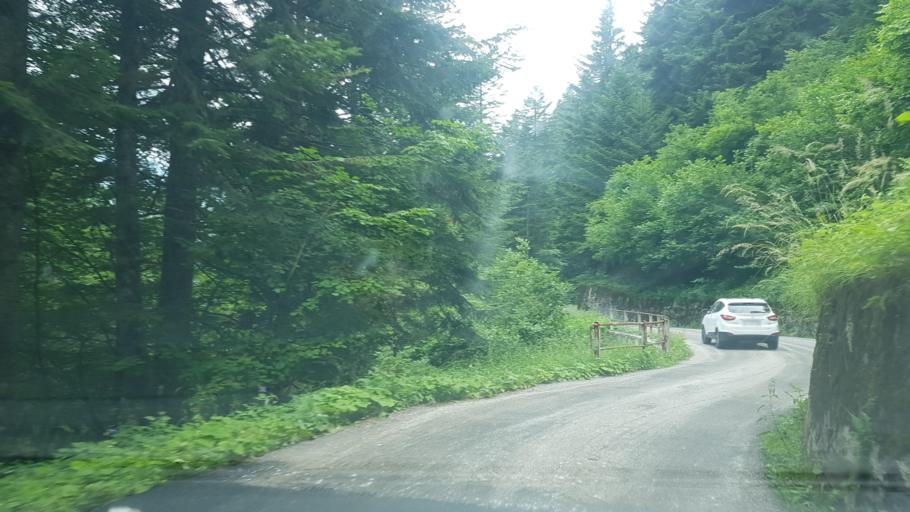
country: IT
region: Friuli Venezia Giulia
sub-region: Provincia di Udine
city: Paularo
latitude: 46.5563
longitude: 13.1284
